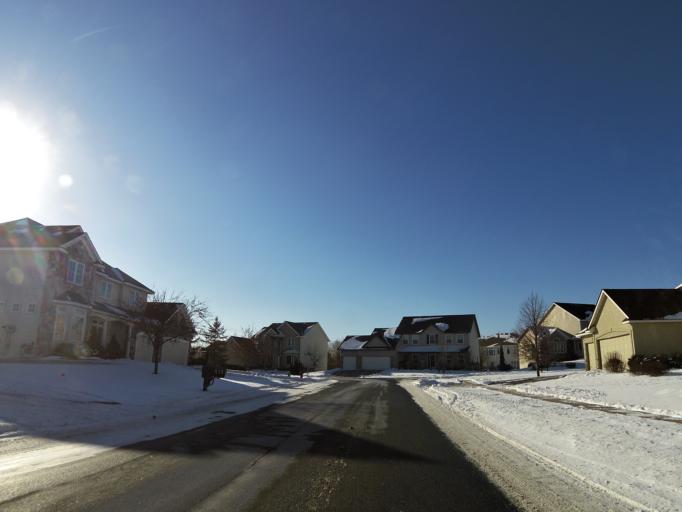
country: US
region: Minnesota
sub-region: Scott County
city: Prior Lake
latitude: 44.7257
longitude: -93.4582
